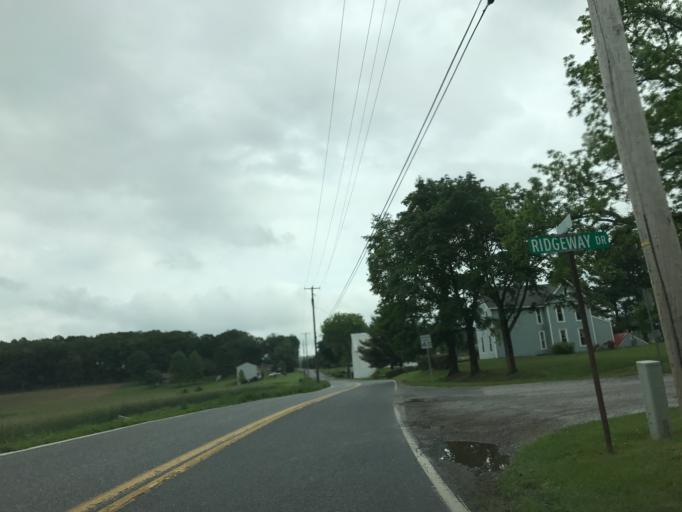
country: US
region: Pennsylvania
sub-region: York County
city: Dallastown
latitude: 39.8422
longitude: -76.6322
